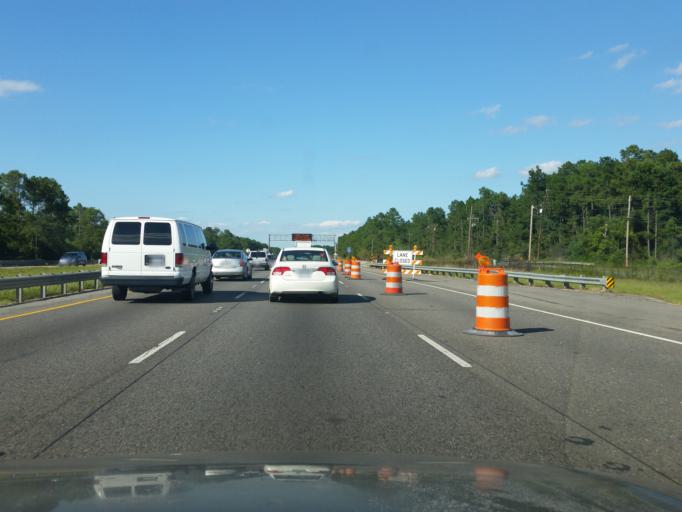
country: US
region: Louisiana
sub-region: Saint Tammany Parish
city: Slidell
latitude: 30.2913
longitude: -89.7470
